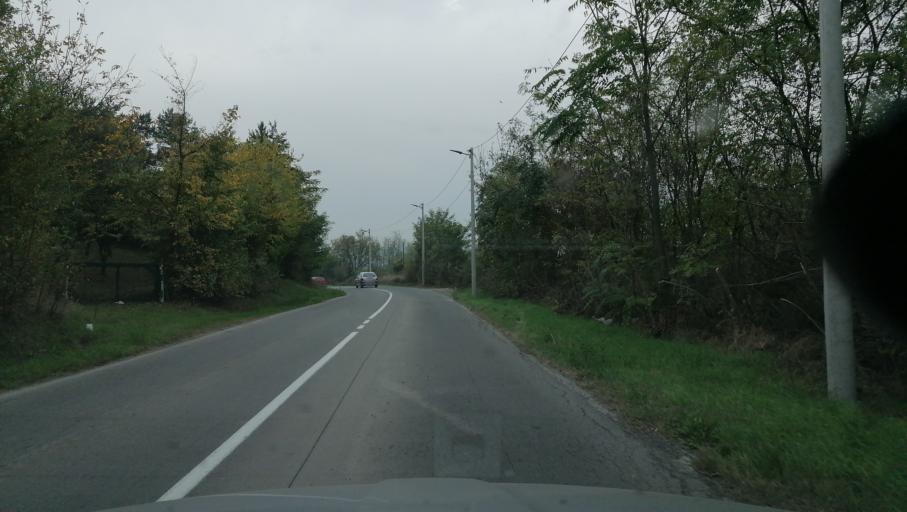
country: RS
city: Rusanj
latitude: 44.6847
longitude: 20.5035
